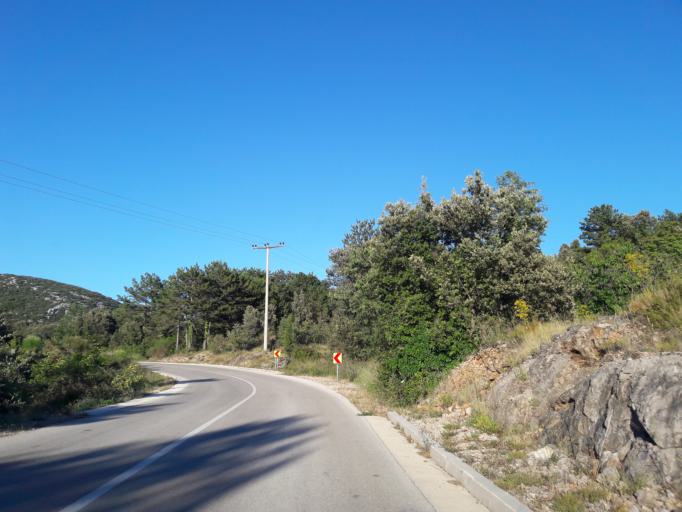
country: HR
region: Dubrovacko-Neretvanska
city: Orebic
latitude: 42.9997
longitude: 17.2528
